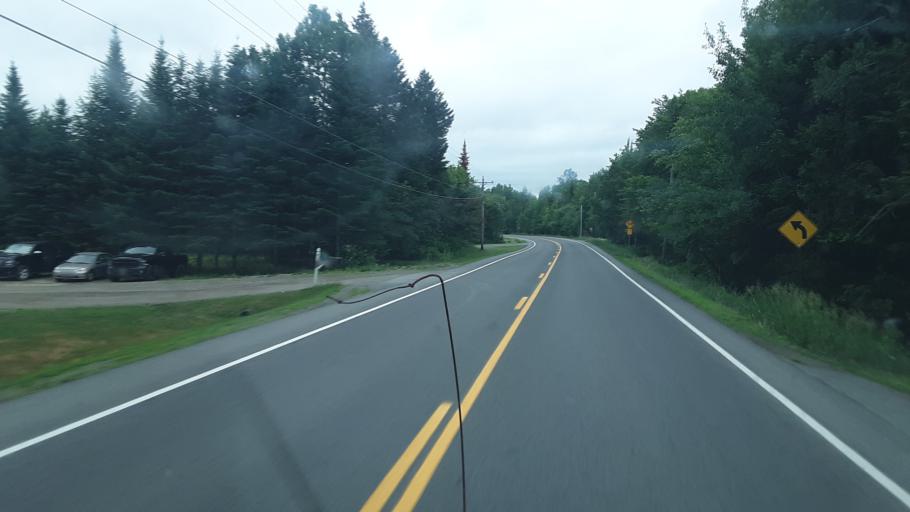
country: US
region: Maine
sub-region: Penobscot County
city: Patten
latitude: 45.9320
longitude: -68.4481
